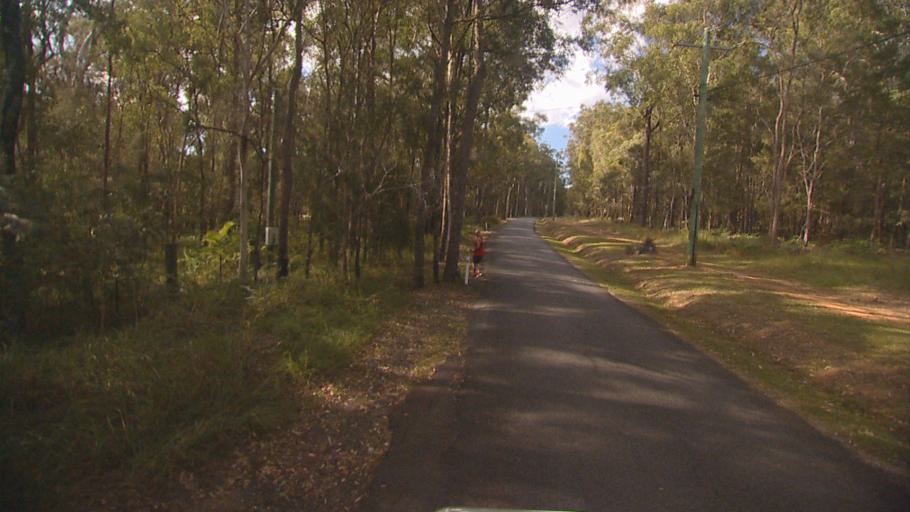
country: AU
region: Queensland
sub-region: Redland
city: Redland Bay
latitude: -27.6536
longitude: 153.2516
